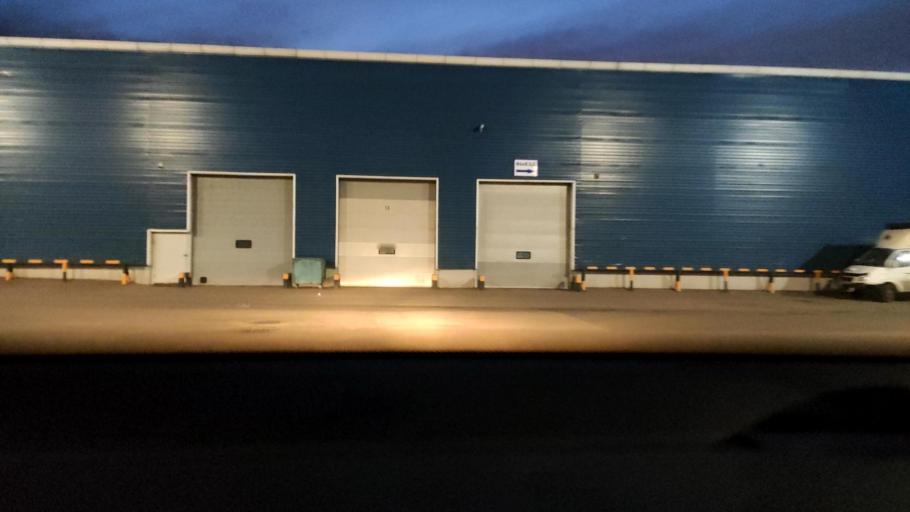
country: RU
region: Moskovskaya
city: Biryulevo Zapadnoye
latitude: 55.5929
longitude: 37.6231
